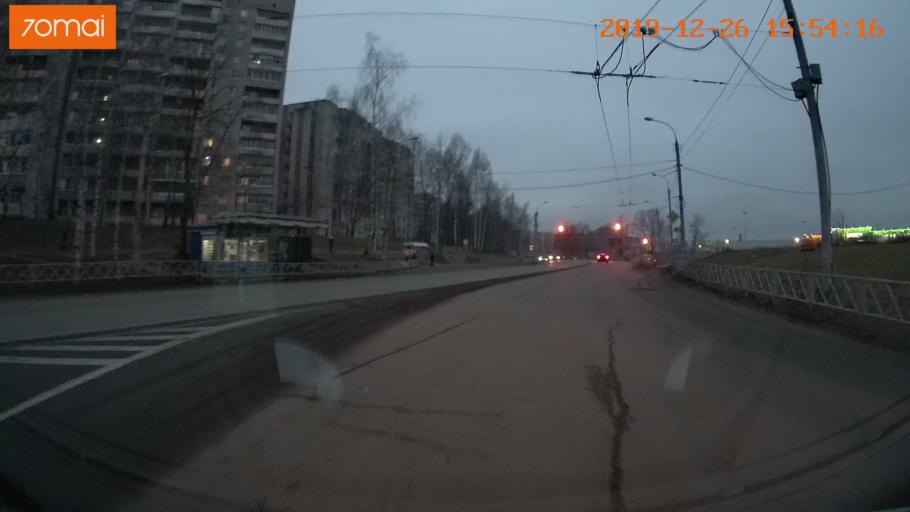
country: RU
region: Jaroslavl
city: Rybinsk
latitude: 58.0455
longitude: 38.8205
